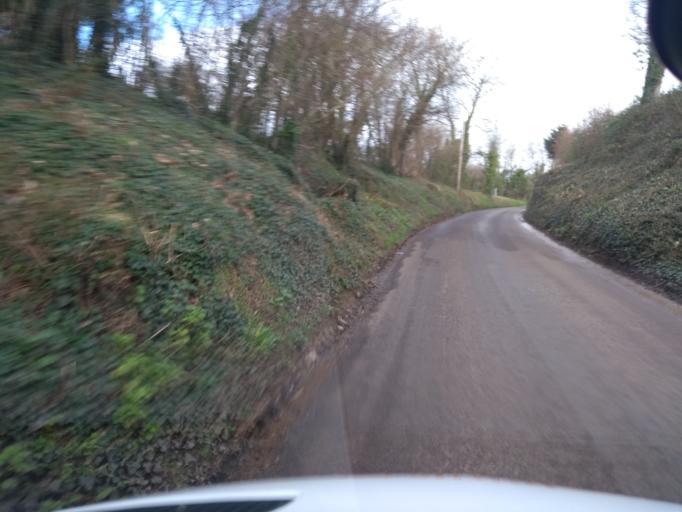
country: GB
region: England
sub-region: Somerset
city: Westonzoyland
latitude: 51.1322
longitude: -2.8638
